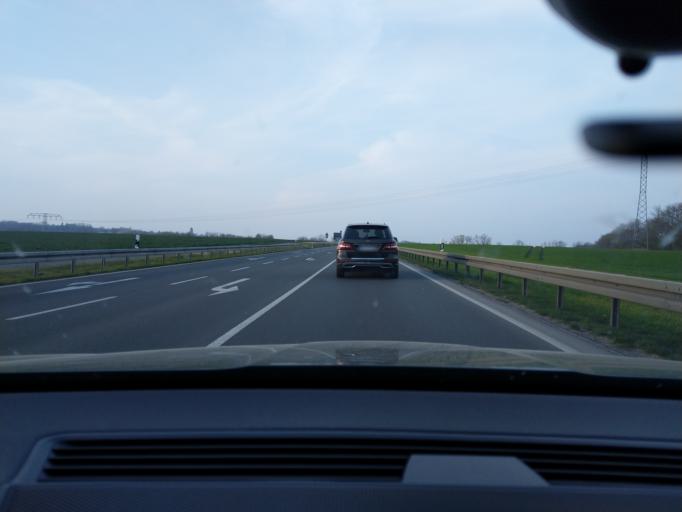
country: DE
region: Mecklenburg-Vorpommern
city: Stralsund
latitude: 54.2878
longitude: 13.0501
